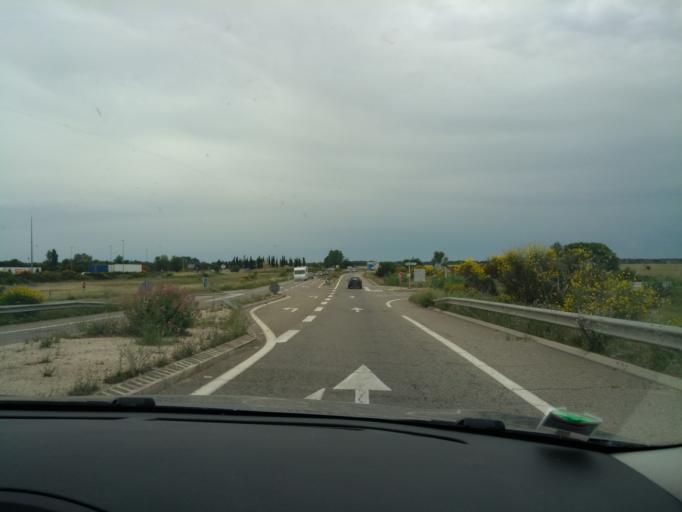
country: FR
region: Provence-Alpes-Cote d'Azur
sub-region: Departement des Bouches-du-Rhone
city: Miramas
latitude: 43.6378
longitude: 5.0215
